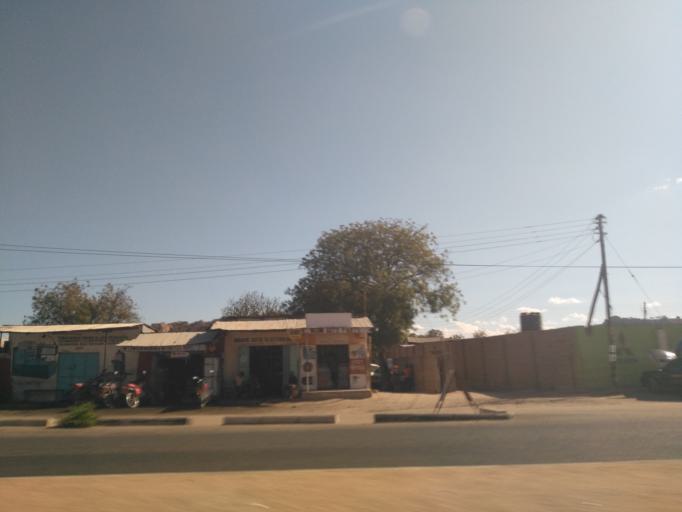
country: TZ
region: Dodoma
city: Dodoma
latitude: -6.1720
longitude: 35.7322
